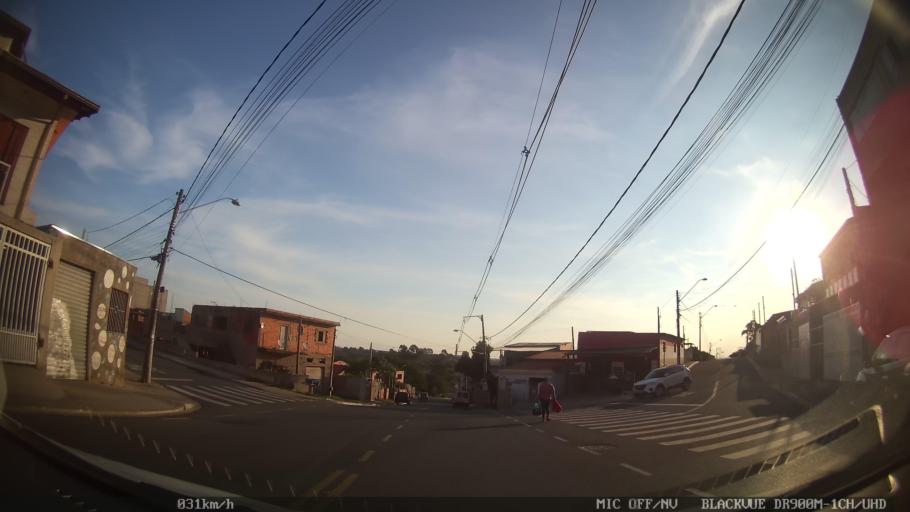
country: BR
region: Sao Paulo
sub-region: Campinas
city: Campinas
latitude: -22.9912
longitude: -47.1211
